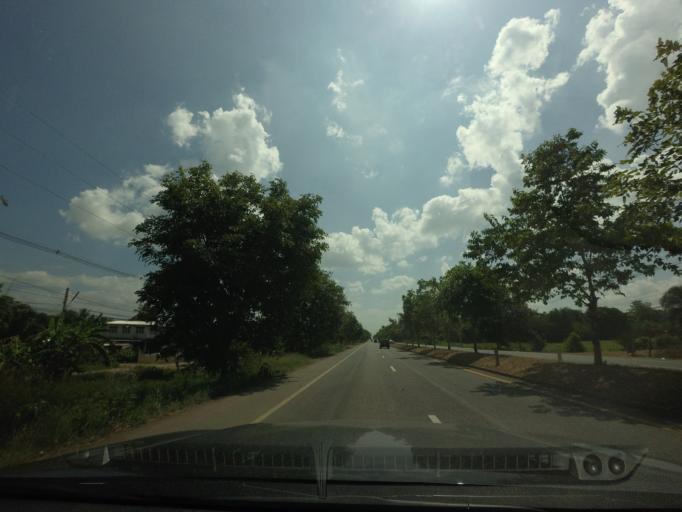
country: TH
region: Phetchabun
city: Nong Phai
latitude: 16.0249
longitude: 101.0746
